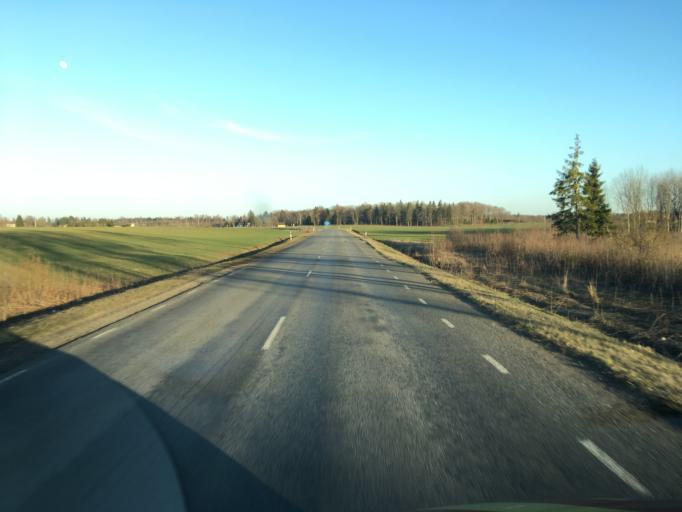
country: EE
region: Raplamaa
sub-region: Kehtna vald
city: Kehtna
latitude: 59.0589
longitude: 24.9409
